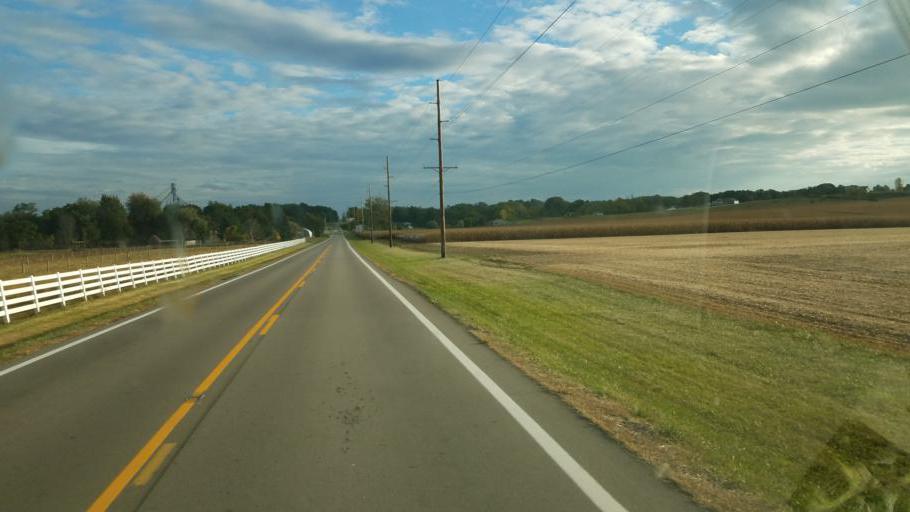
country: US
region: Ohio
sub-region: Ashland County
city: Loudonville
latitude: 40.7791
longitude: -82.1847
